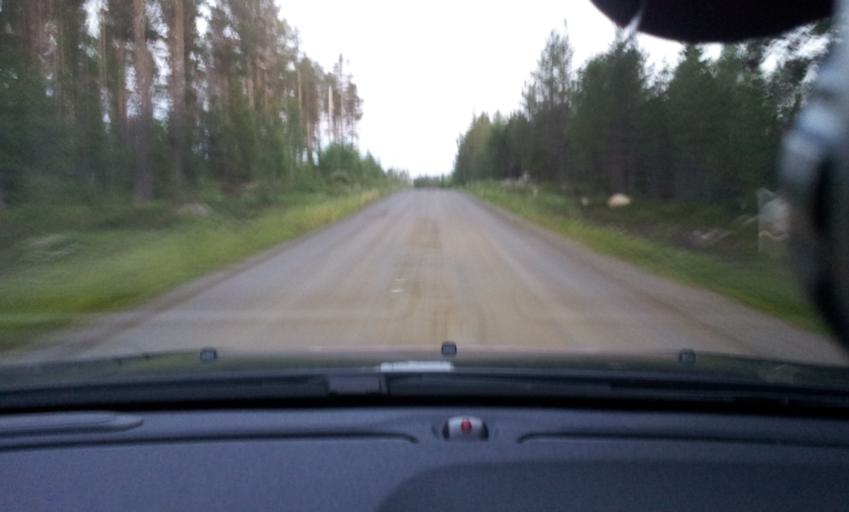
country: SE
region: Vaesternorrland
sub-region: Ange Kommun
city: Fransta
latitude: 62.8511
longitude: 16.0219
